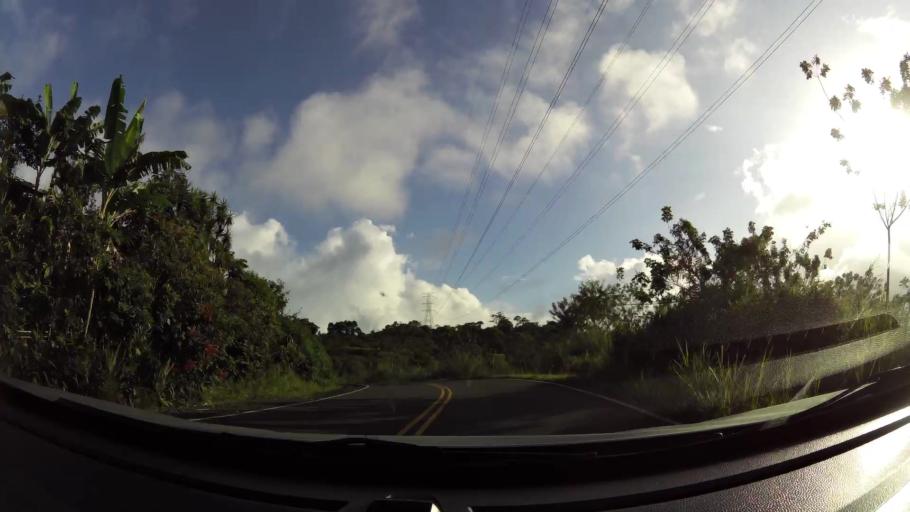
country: CR
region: Limon
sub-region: Canton de Siquirres
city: Siquirres
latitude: 10.0420
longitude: -83.5484
